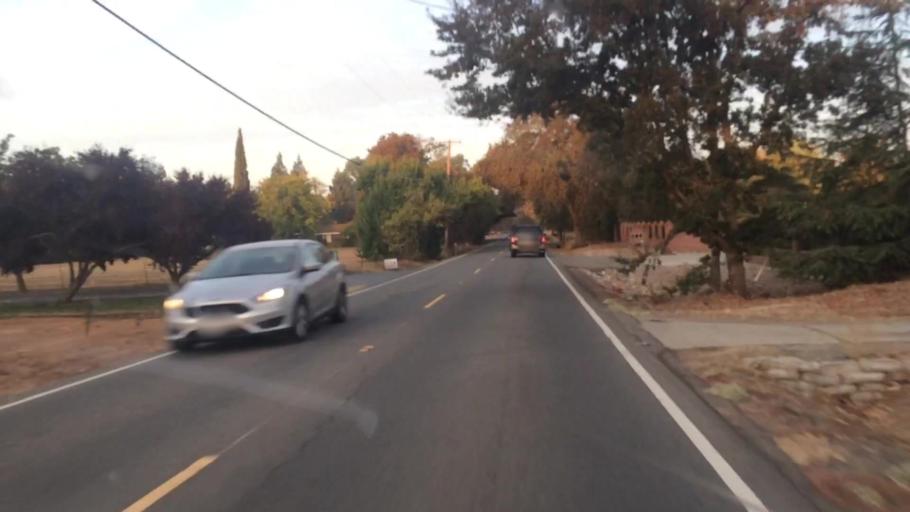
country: US
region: California
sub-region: Sacramento County
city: Vineyard
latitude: 38.4382
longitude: -121.3141
